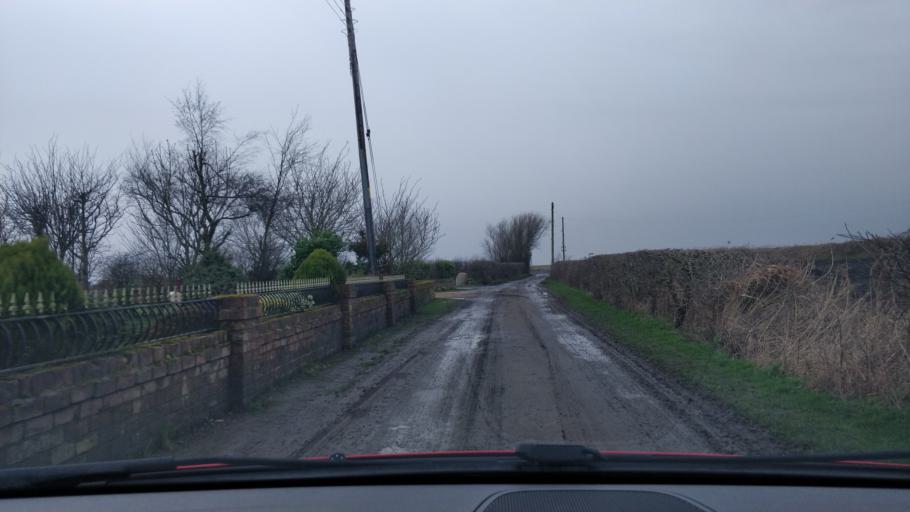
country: GB
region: England
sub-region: Lancashire
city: Banks
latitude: 53.6864
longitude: -2.9335
